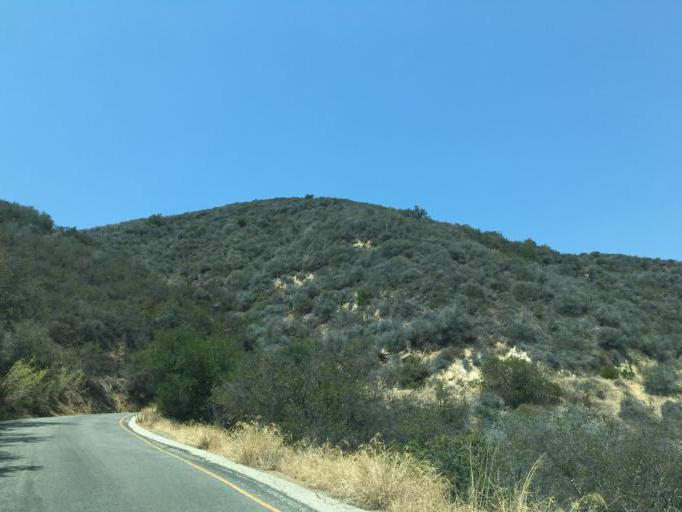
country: US
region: California
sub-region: Los Angeles County
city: Las Flores
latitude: 34.0498
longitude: -118.5962
